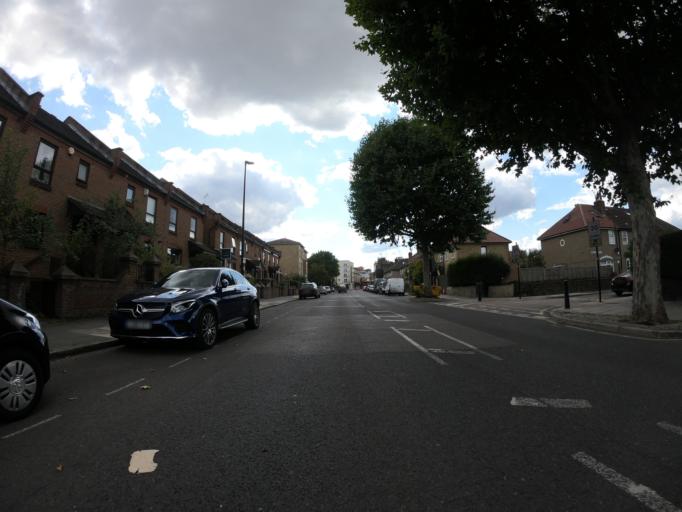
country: GB
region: England
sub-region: Greater London
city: Poplar
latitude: 51.4875
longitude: -0.0111
